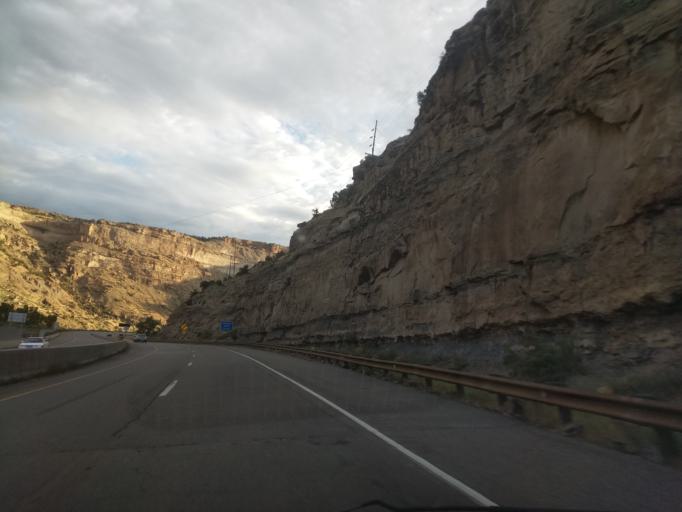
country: US
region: Colorado
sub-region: Mesa County
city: Palisade
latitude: 39.1887
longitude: -108.2804
